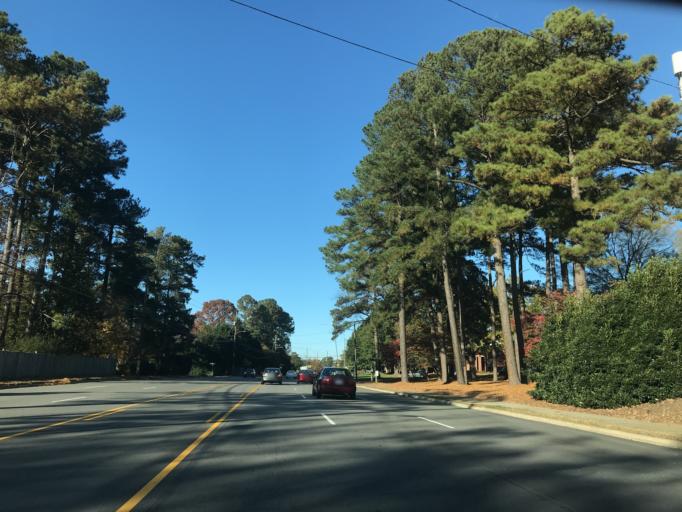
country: US
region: North Carolina
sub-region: Wake County
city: West Raleigh
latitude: 35.8469
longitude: -78.6148
